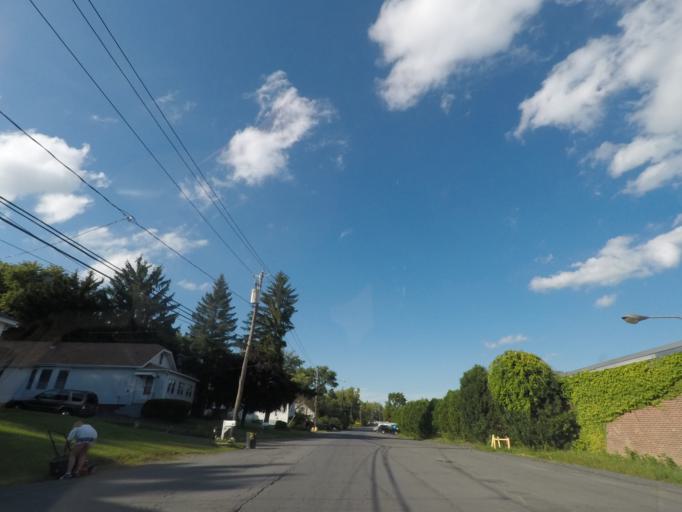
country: US
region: New York
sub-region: Albany County
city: Watervliet
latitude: 42.7386
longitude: -73.7117
